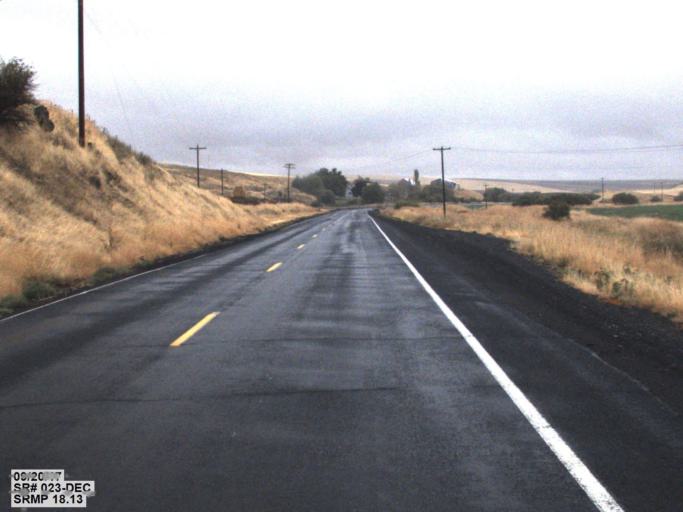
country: US
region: Washington
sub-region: Whitman County
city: Colfax
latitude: 47.1159
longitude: -117.6528
